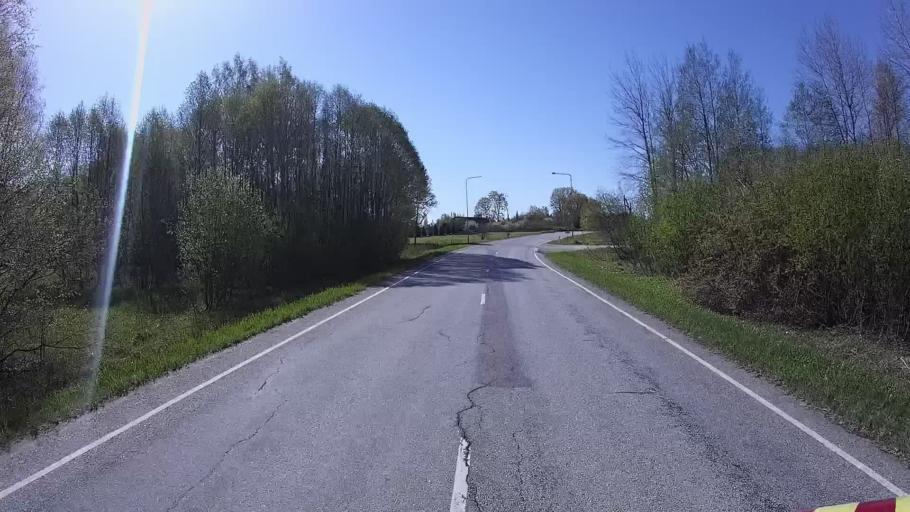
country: EE
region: Raplamaa
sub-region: Jaervakandi vald
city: Jarvakandi
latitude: 58.7936
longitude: 24.8184
